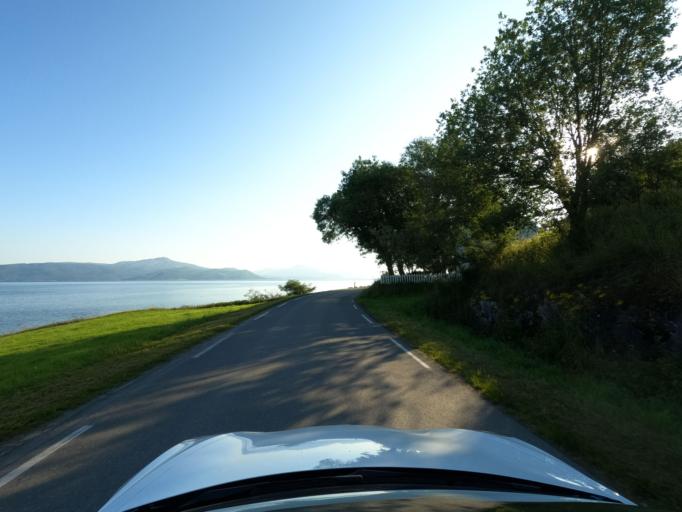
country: NO
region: Nordland
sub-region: Ballangen
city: Ballangen
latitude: 68.4690
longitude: 16.8588
